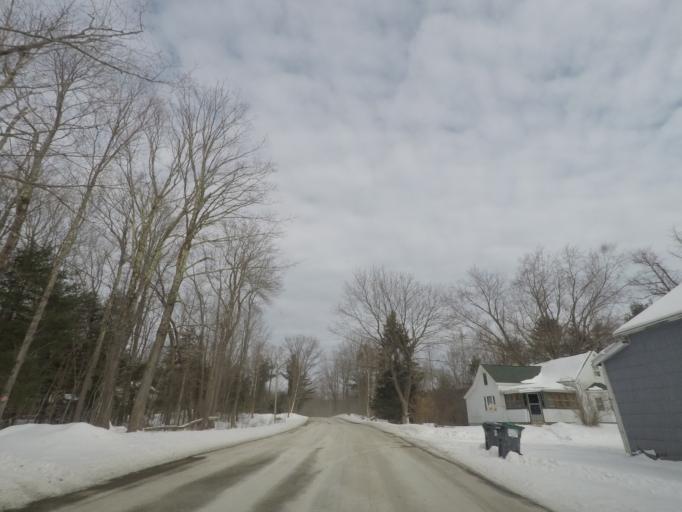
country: US
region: New York
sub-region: Rensselaer County
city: Averill Park
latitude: 42.6026
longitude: -73.4815
